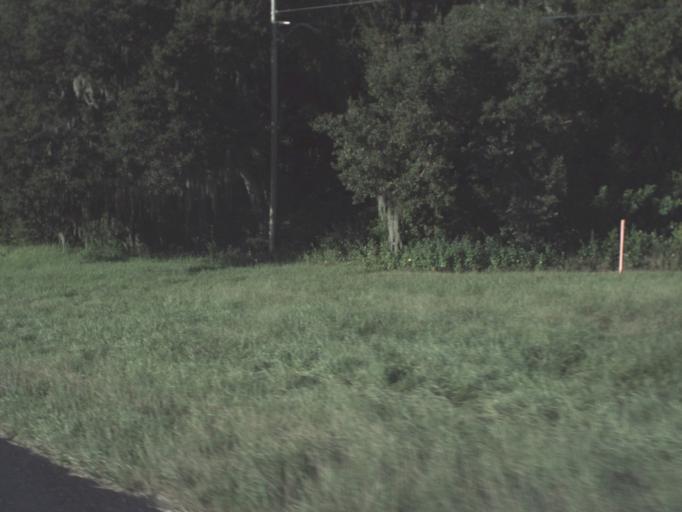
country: US
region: Florida
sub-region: Polk County
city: Fort Meade
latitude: 27.8126
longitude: -81.8208
